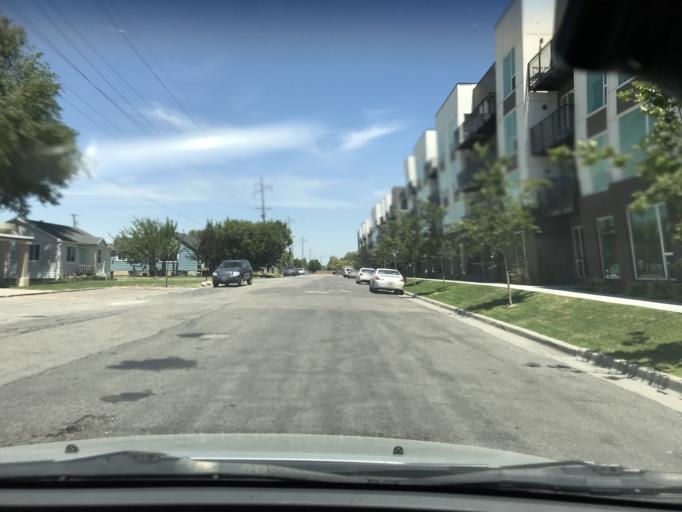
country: US
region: Utah
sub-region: Salt Lake County
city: Salt Lake City
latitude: 40.7697
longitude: -111.9439
